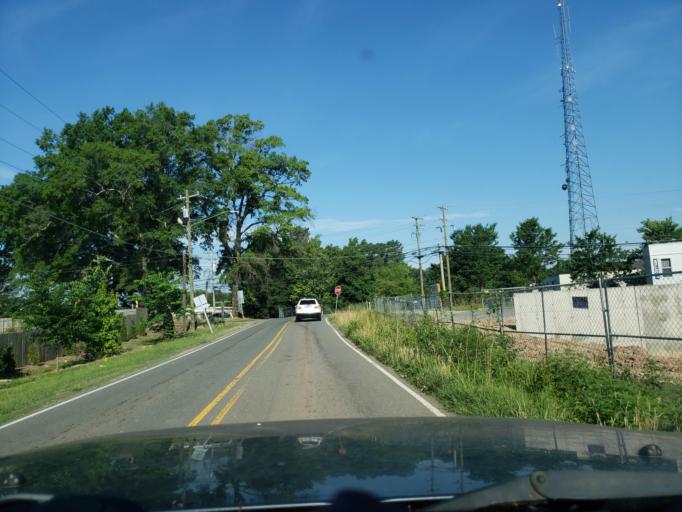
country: US
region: North Carolina
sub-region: Durham County
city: Durham
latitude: 35.9611
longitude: -78.8703
